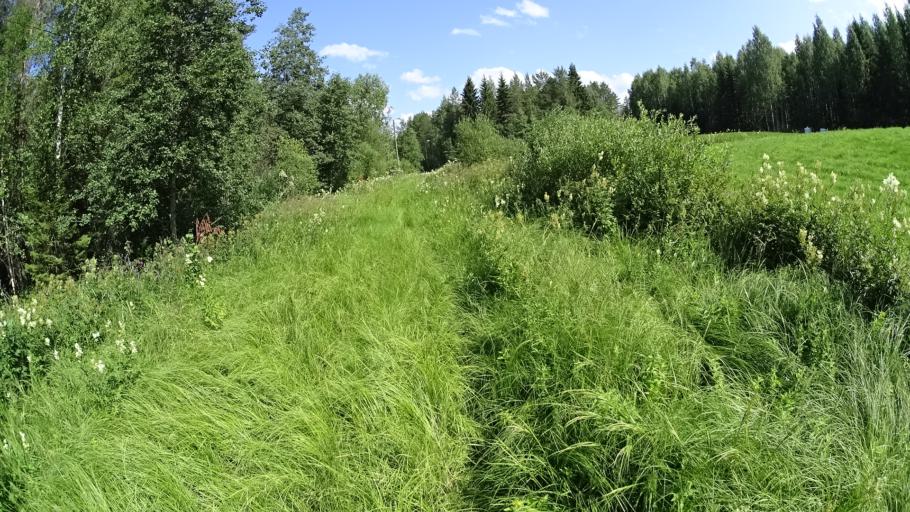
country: FI
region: North Karelia
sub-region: Pielisen Karjala
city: Lieksa
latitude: 63.1171
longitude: 29.7922
